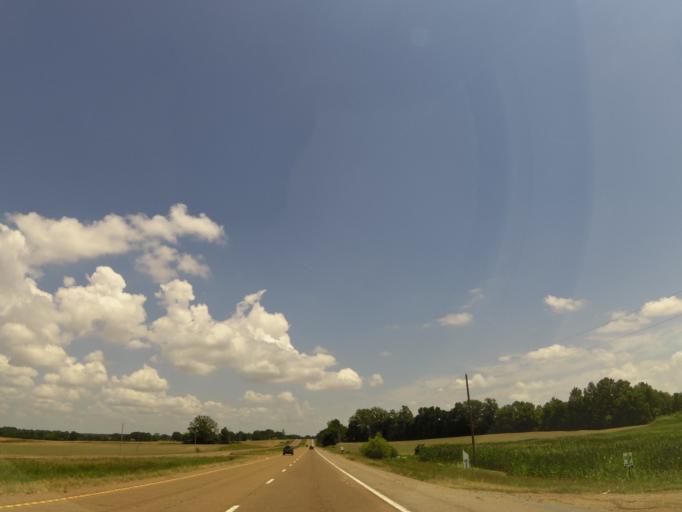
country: US
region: Tennessee
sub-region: Lauderdale County
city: Halls
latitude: 35.9456
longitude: -89.3055
